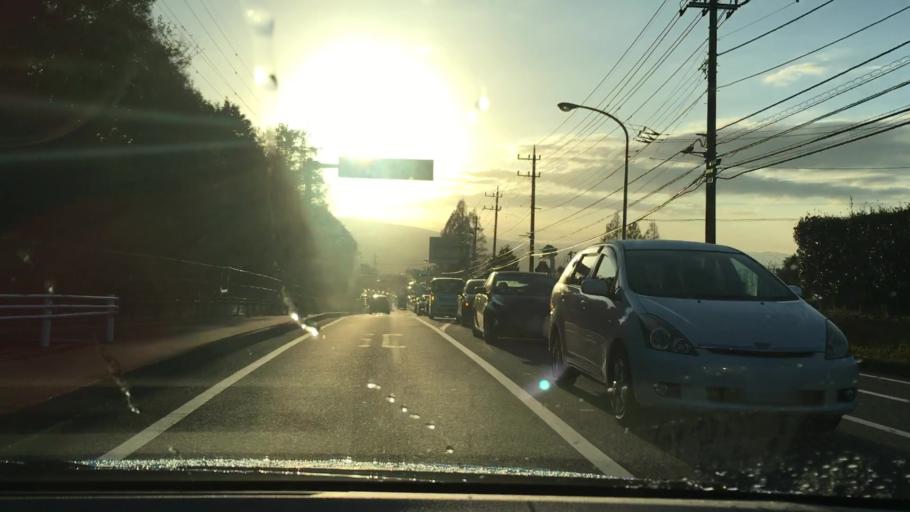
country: JP
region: Shizuoka
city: Gotemba
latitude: 35.2247
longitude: 138.8944
